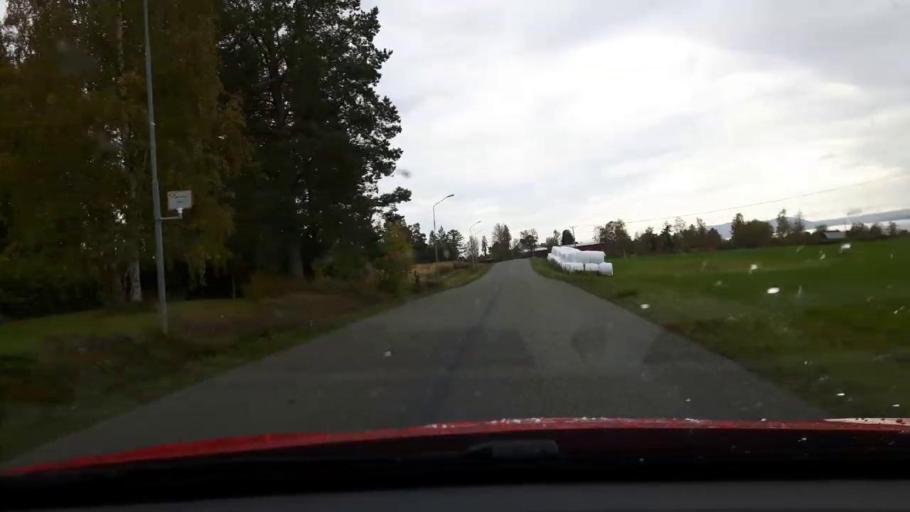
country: SE
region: Jaemtland
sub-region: Bergs Kommun
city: Hoverberg
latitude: 62.9507
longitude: 14.4907
